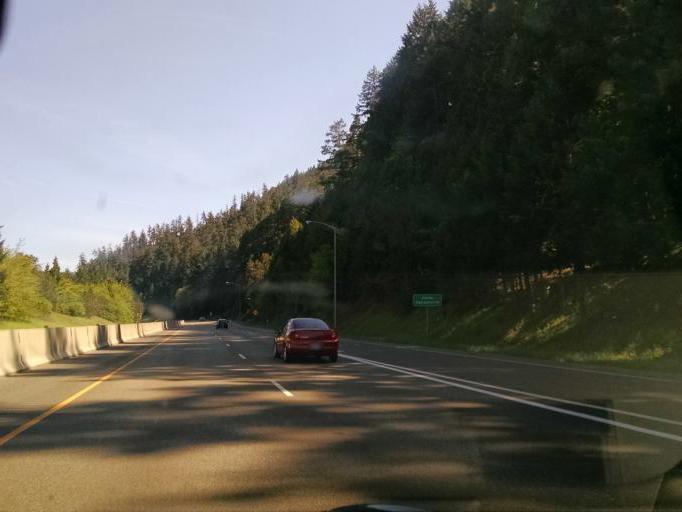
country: US
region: Oregon
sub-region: Douglas County
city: Canyonville
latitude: 42.9210
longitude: -123.2764
